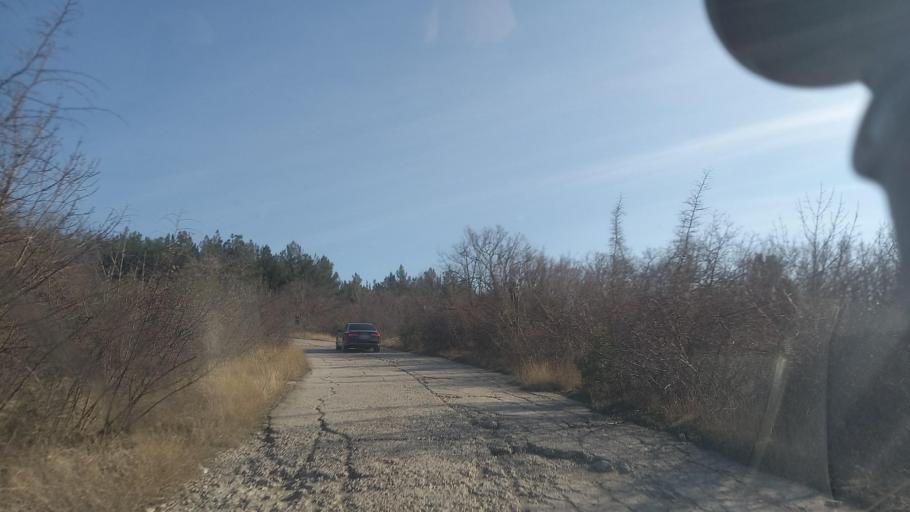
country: RU
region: Krasnodarskiy
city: Kabardinka
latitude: 44.6295
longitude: 37.9123
